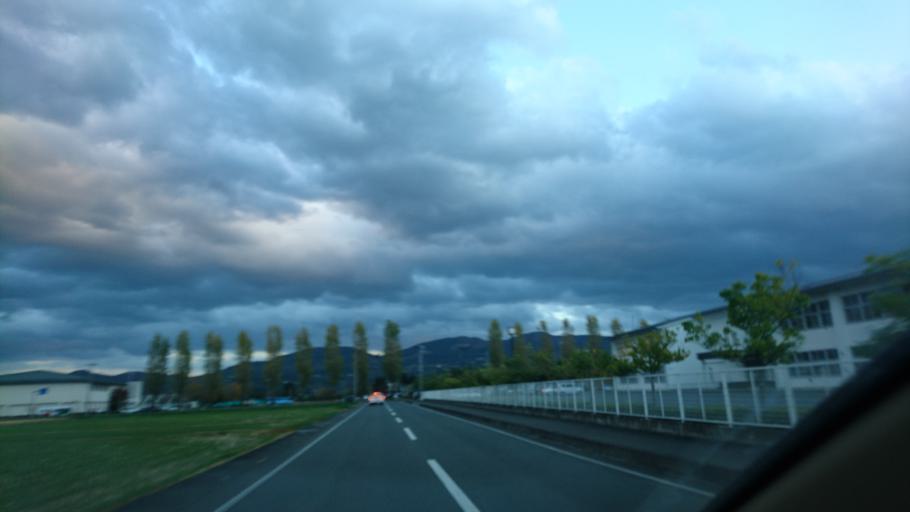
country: JP
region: Iwate
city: Mizusawa
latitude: 39.0587
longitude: 141.1395
